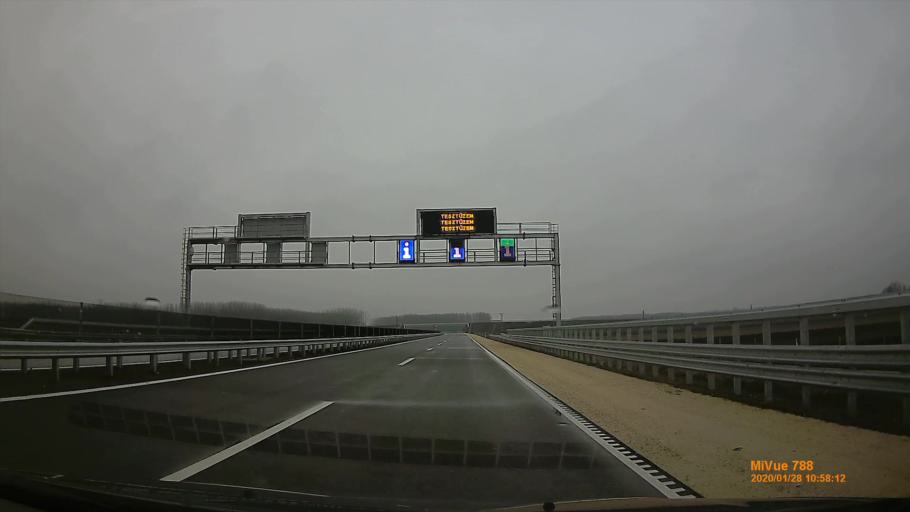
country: HU
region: Pest
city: Peteri
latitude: 47.3759
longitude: 19.4037
